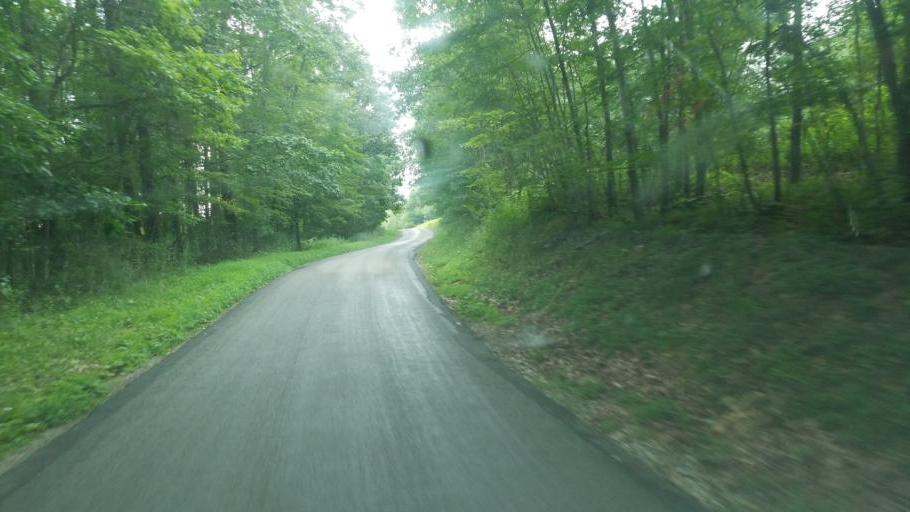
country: US
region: Pennsylvania
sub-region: Clarion County
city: Clarion
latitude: 41.1768
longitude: -79.3804
